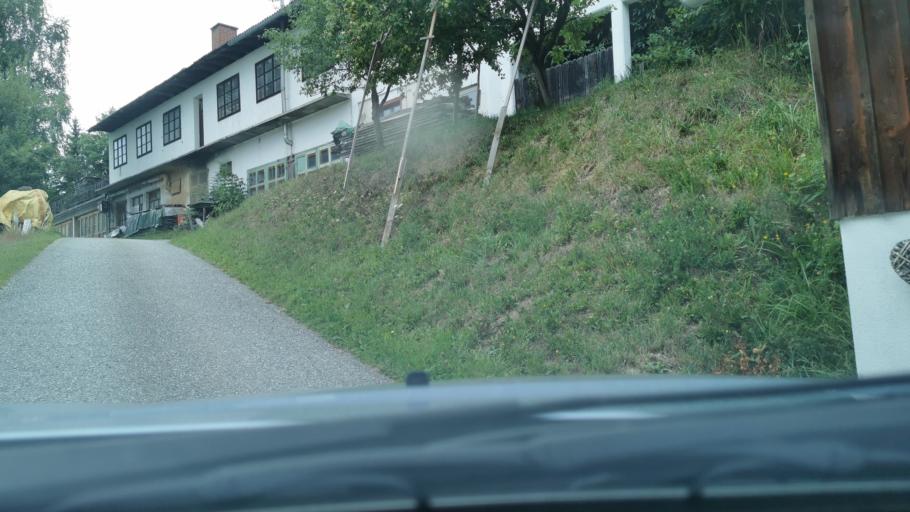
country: AT
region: Styria
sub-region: Politischer Bezirk Weiz
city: Fischbach
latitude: 47.3932
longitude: 15.6701
